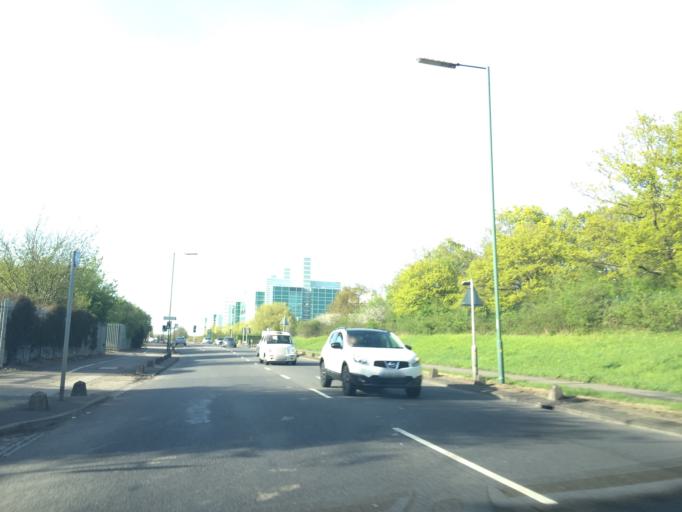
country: GB
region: England
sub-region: Essex
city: Roydon
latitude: 51.7635
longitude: 0.0675
